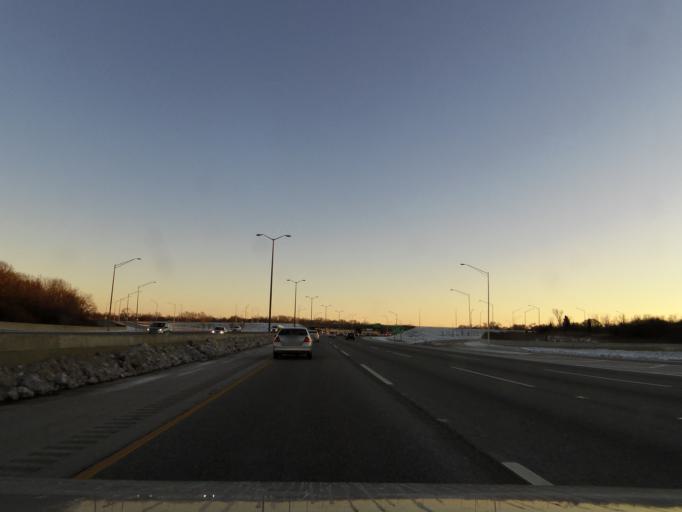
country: US
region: Illinois
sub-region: DuPage County
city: Oak Brook
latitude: 41.8220
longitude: -87.9160
